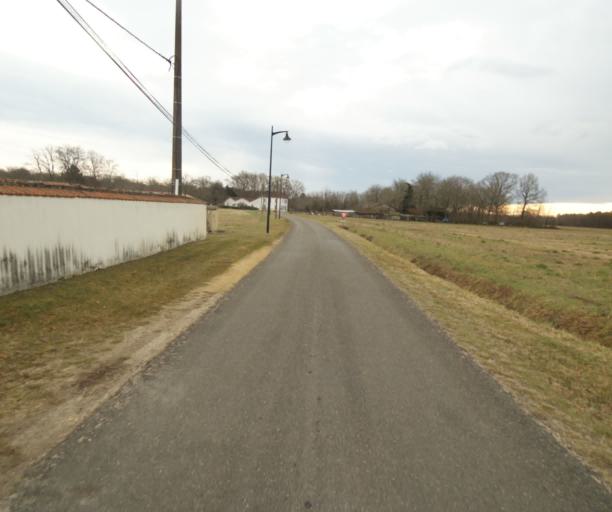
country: FR
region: Aquitaine
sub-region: Departement des Landes
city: Gabarret
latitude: 44.0110
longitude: -0.0244
